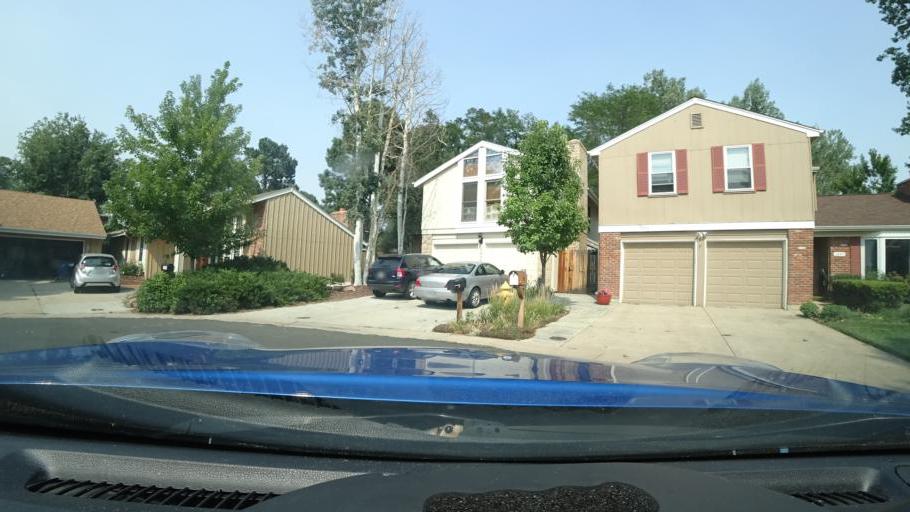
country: US
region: Colorado
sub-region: Adams County
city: Aurora
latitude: 39.6655
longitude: -104.8544
